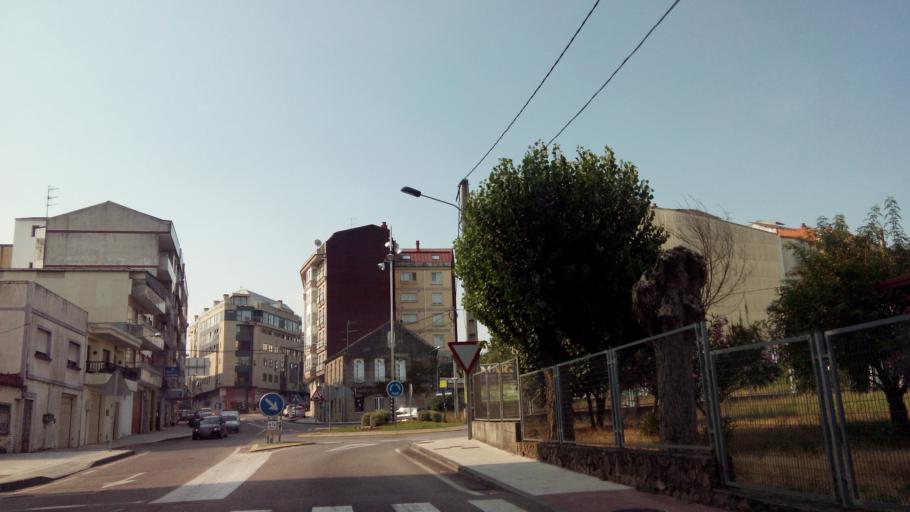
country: ES
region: Galicia
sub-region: Provincia de Pontevedra
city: Ponteareas
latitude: 42.1695
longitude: -8.5064
